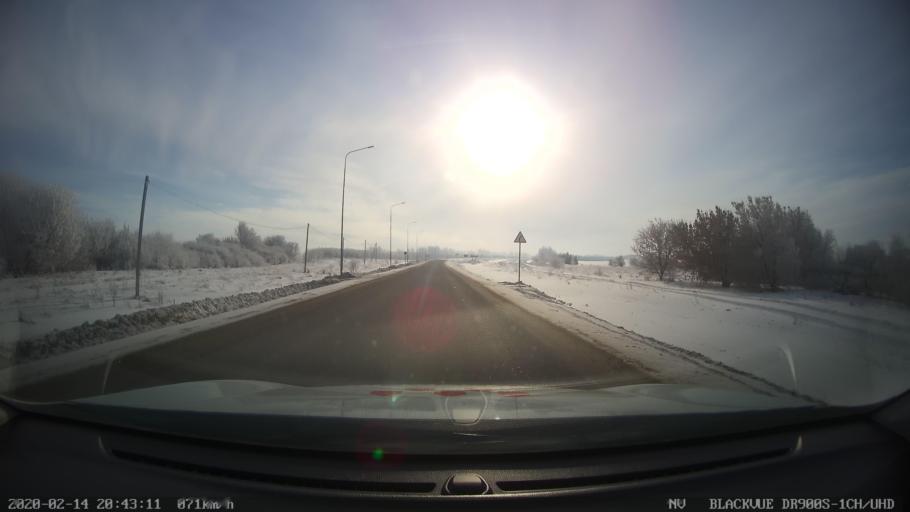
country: RU
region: Tatarstan
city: Kuybyshevskiy Zaton
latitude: 55.3107
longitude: 49.1458
